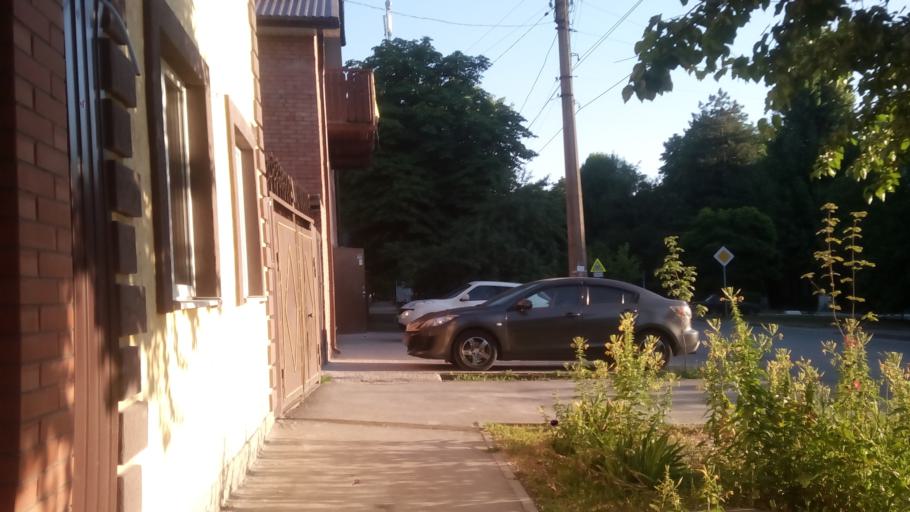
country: RU
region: Rostov
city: Imeni Chkalova
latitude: 47.2469
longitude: 39.7677
